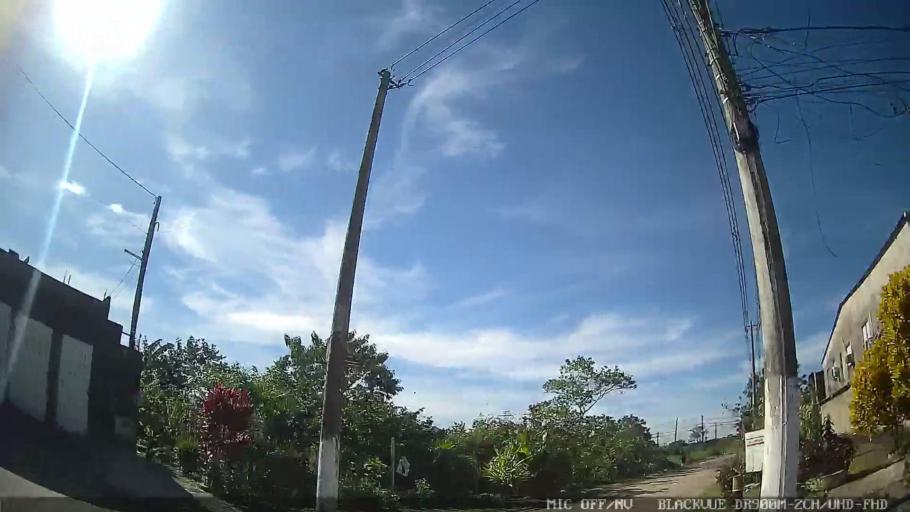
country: BR
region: Sao Paulo
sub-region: Santos
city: Santos
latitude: -23.9353
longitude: -46.2841
